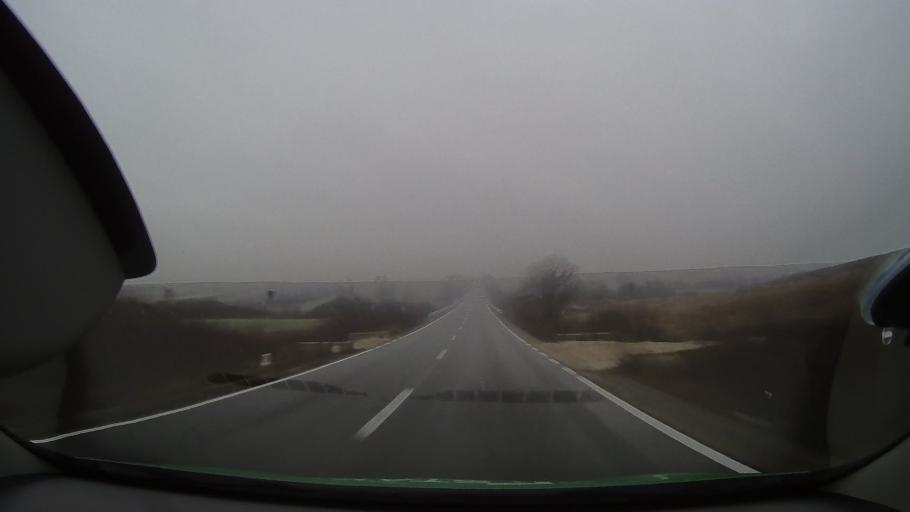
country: RO
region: Bihor
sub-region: Comuna Olcea
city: Olcea
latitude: 46.6802
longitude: 21.9660
